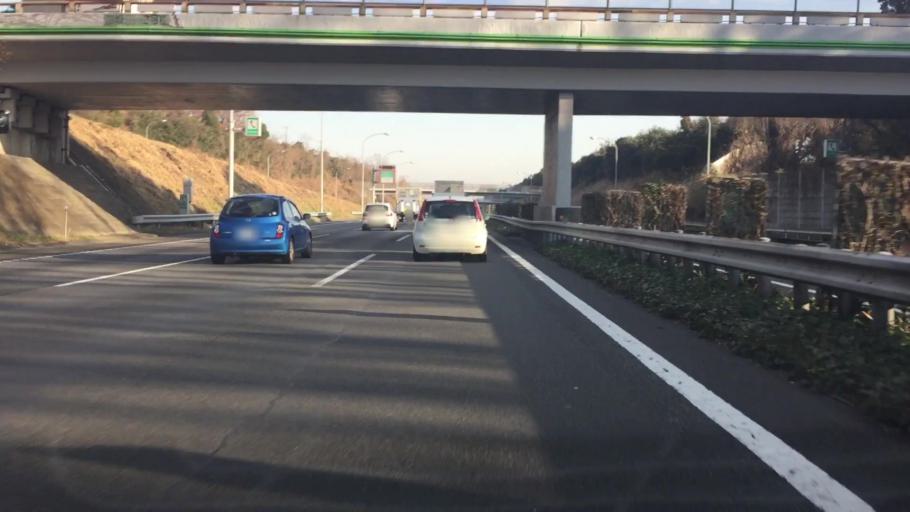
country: JP
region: Saitama
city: Sakado
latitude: 35.9879
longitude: 139.3833
